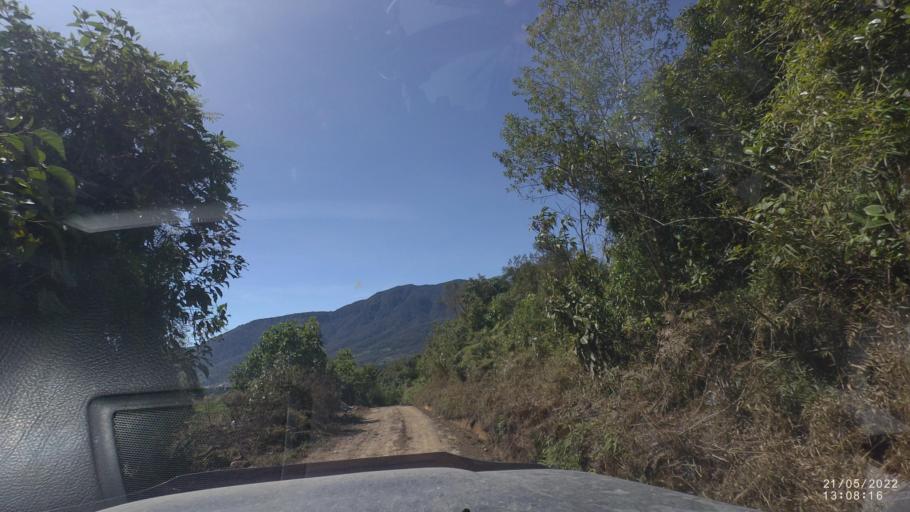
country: BO
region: Cochabamba
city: Colomi
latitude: -17.1481
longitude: -65.9433
